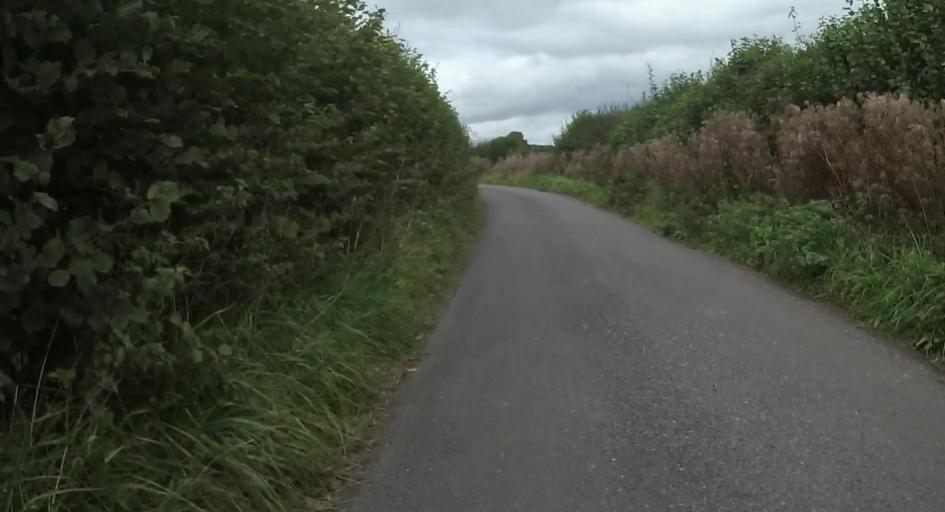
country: GB
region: England
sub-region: Hampshire
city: Alton
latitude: 51.1168
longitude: -0.9746
